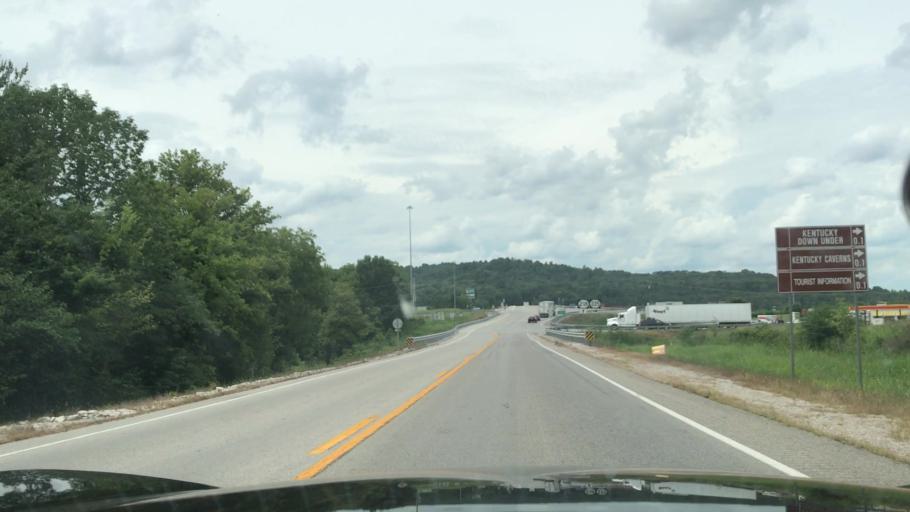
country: US
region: Kentucky
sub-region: Hart County
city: Horse Cave
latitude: 37.1991
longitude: -85.9337
